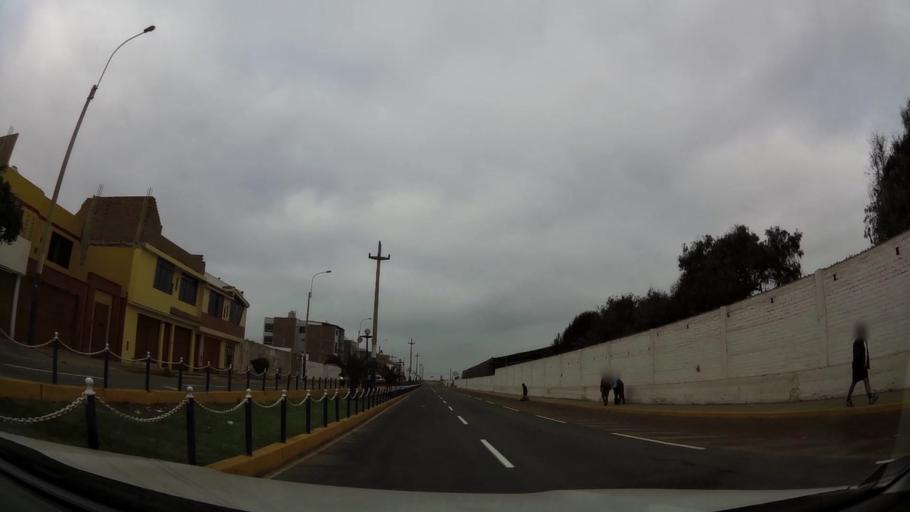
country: PE
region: Lima
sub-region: Lima
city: Surco
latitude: -12.2080
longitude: -77.0192
